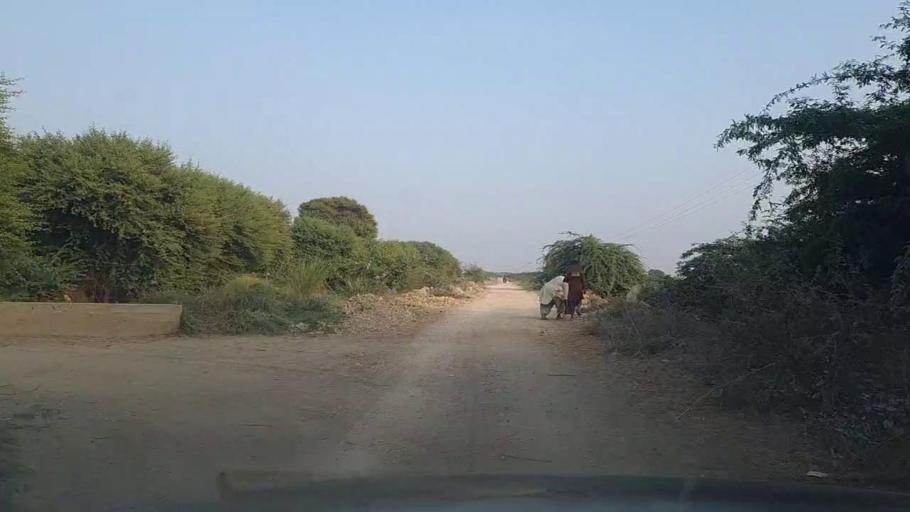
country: PK
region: Sindh
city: Mirpur Batoro
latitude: 24.5468
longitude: 68.3499
